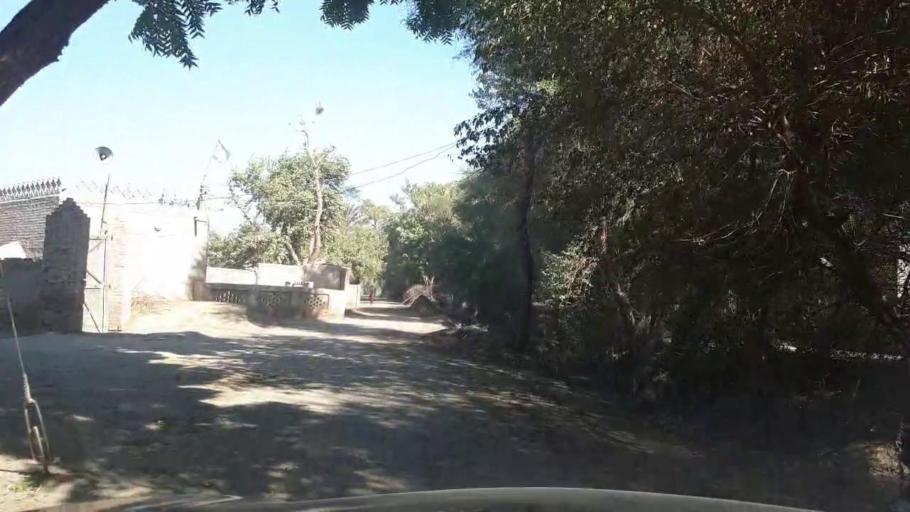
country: PK
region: Sindh
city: Ghotki
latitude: 27.9819
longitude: 69.4246
